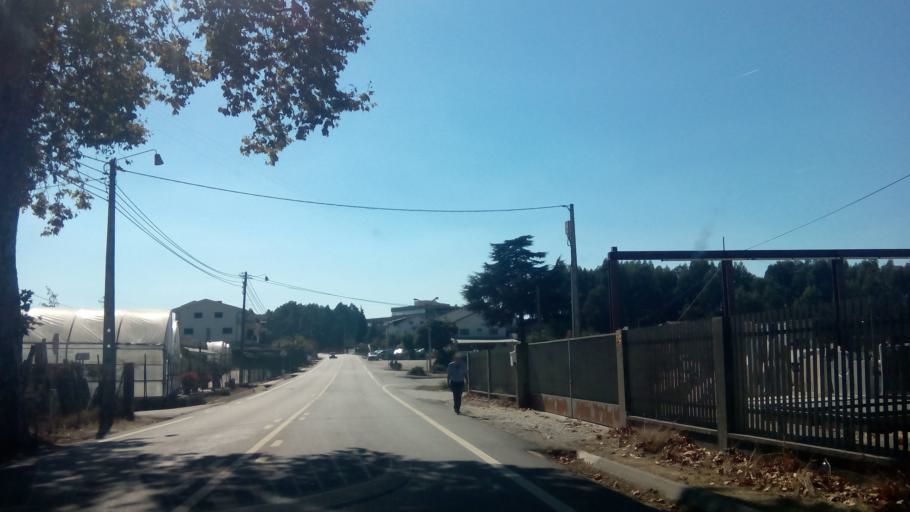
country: PT
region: Porto
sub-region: Lousada
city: Meinedo
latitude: 41.2563
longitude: -8.2125
